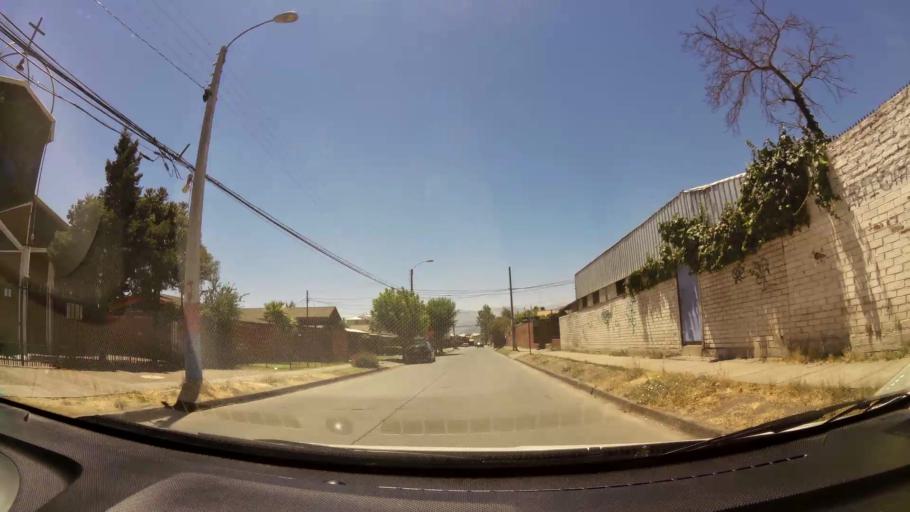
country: CL
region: O'Higgins
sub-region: Provincia de Cachapoal
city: Rancagua
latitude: -34.1582
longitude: -70.7030
